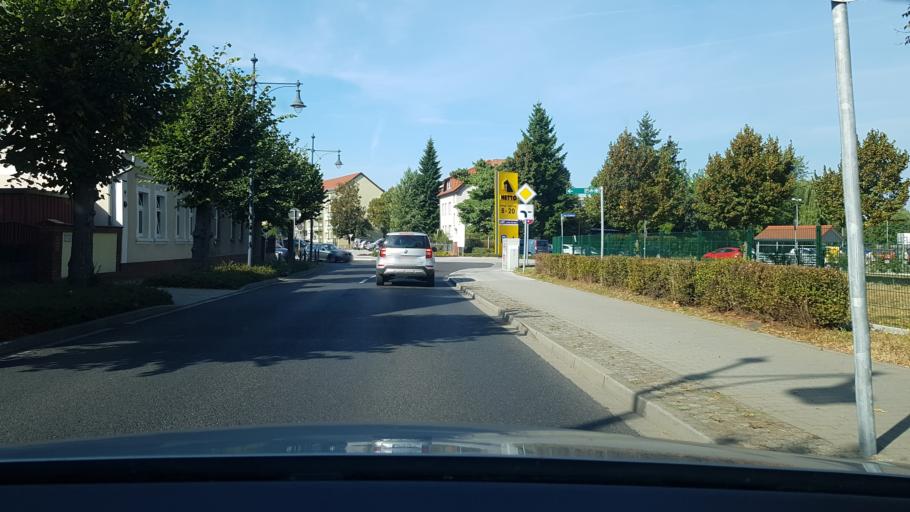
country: DE
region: Brandenburg
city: Beeskow
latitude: 52.1741
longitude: 14.2434
